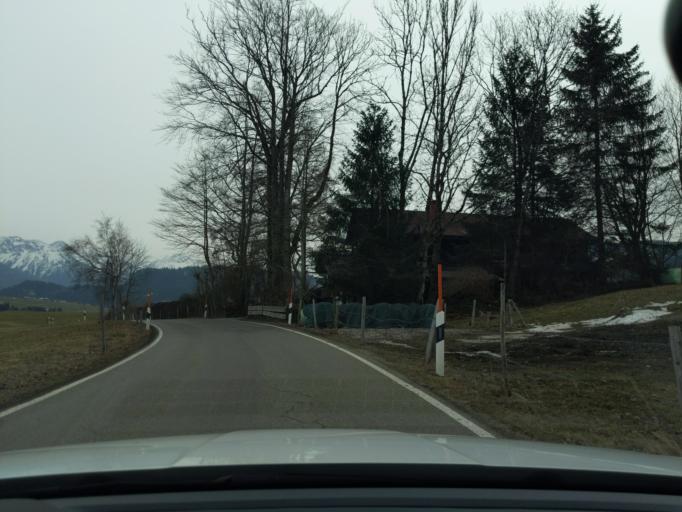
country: DE
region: Bavaria
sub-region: Swabia
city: Bolsterlang
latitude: 47.4644
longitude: 10.2313
